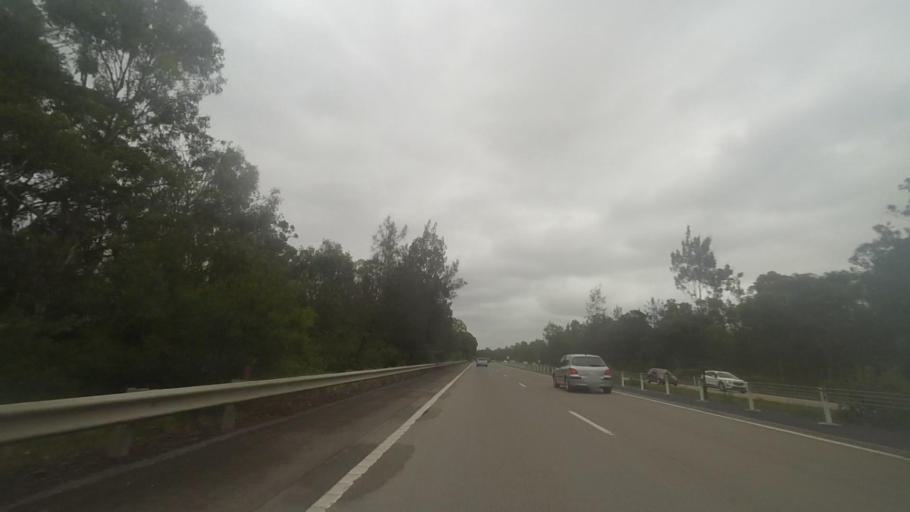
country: AU
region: New South Wales
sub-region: Port Stephens Shire
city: Raymond Terrace
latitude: -32.6995
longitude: 151.8043
